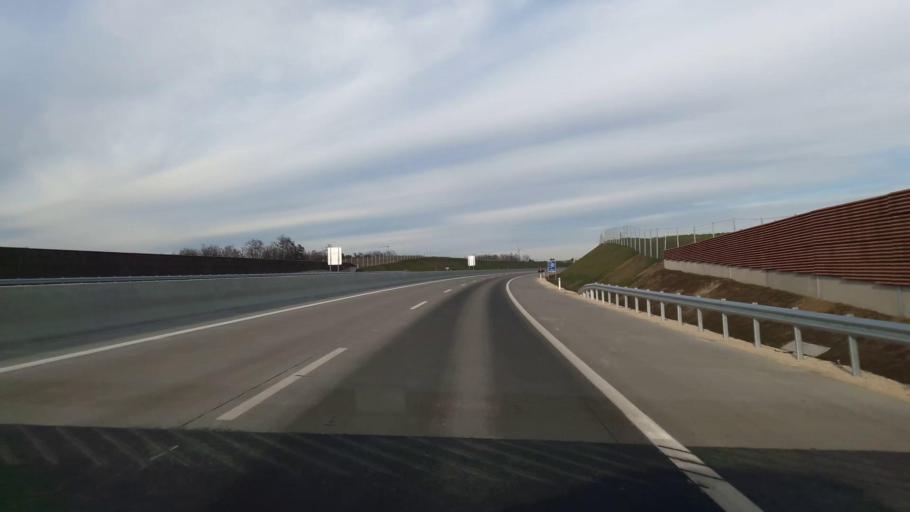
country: AT
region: Lower Austria
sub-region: Politischer Bezirk Mistelbach
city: Wilfersdorf
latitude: 48.5806
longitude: 16.6242
